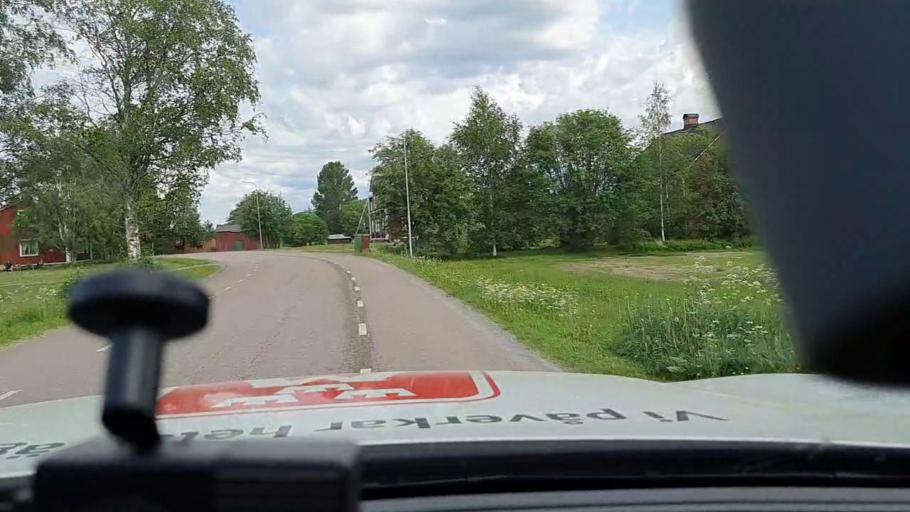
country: SE
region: Norrbotten
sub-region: Bodens Kommun
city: Saevast
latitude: 65.6834
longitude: 21.7980
